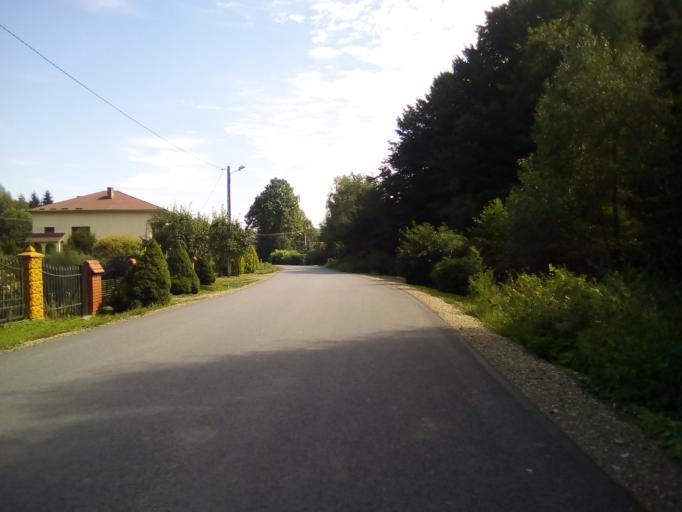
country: PL
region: Subcarpathian Voivodeship
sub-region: Powiat brzozowski
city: Domaradz
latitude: 49.8094
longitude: 21.9270
